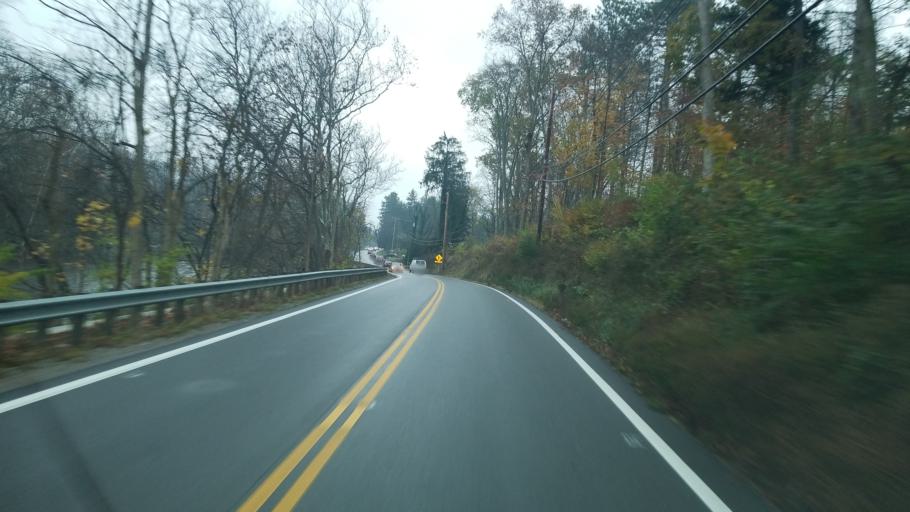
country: US
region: Ohio
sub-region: Delaware County
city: Powell
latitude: 40.1509
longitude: -83.0445
